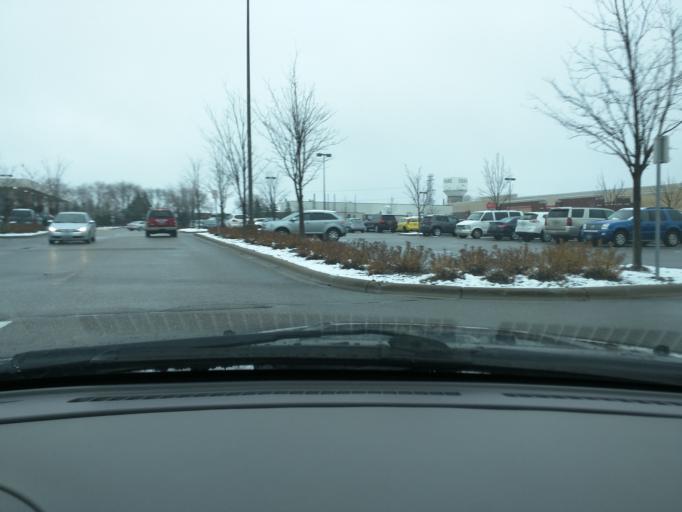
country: US
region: Minnesota
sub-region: Hennepin County
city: Eden Prairie
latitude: 44.8613
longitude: -93.4370
